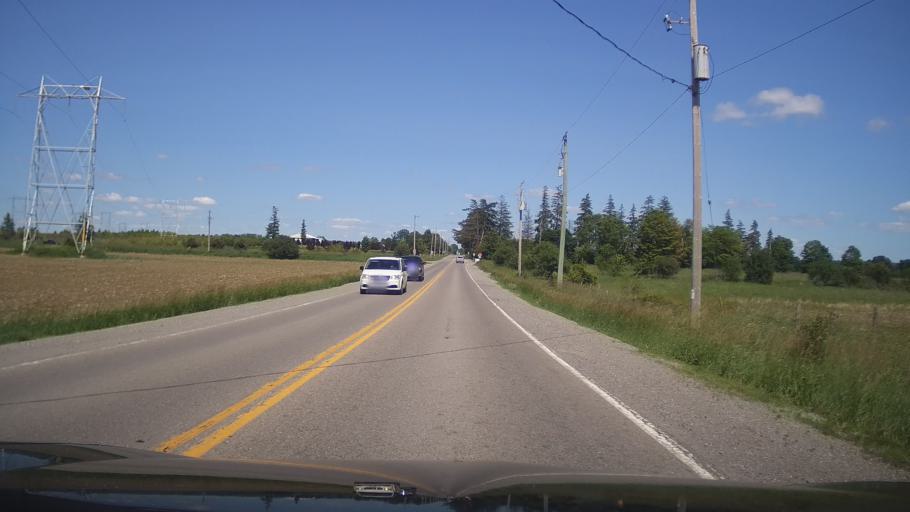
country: CA
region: Ontario
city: Oshawa
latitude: 44.0011
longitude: -78.8312
